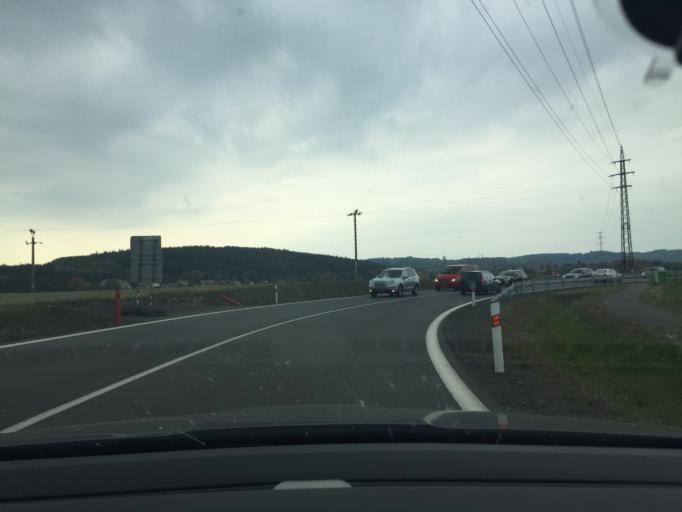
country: CZ
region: Central Bohemia
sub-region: Okres Pribram
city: Pribram
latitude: 49.7044
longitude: 14.0897
